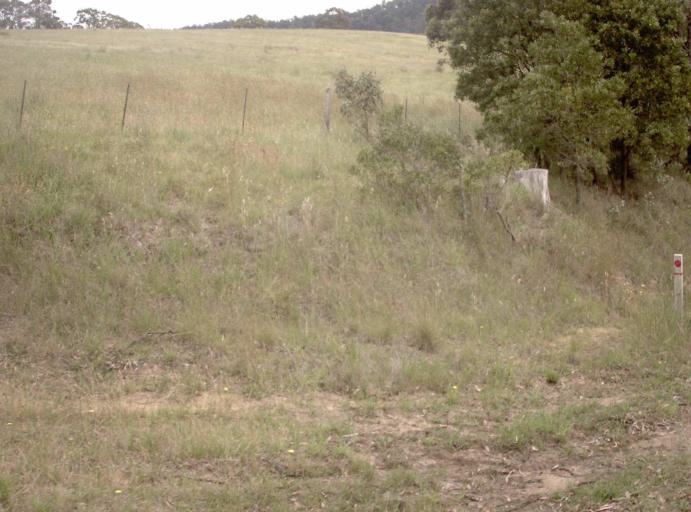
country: AU
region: Victoria
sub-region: East Gippsland
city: Bairnsdale
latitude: -37.5787
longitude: 147.1836
